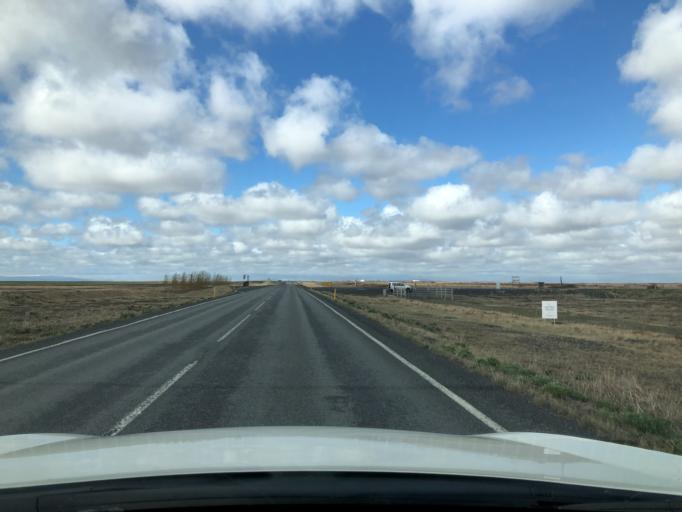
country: IS
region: South
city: Vestmannaeyjar
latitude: 63.7811
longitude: -20.2864
